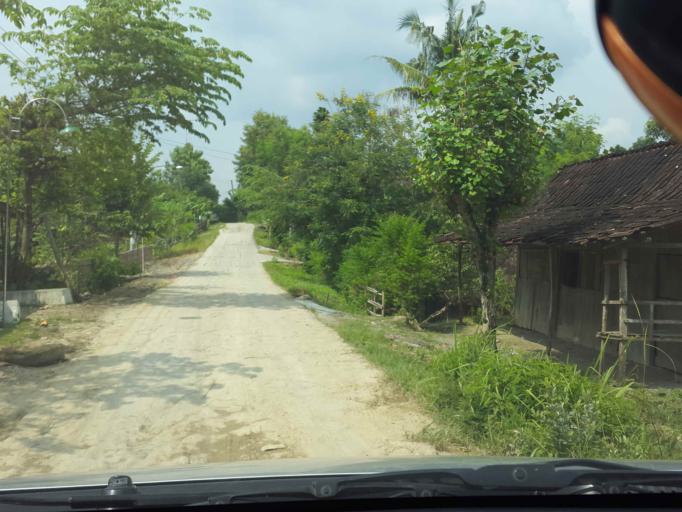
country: ID
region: Central Java
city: Sragen
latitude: -7.3010
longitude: 110.8631
